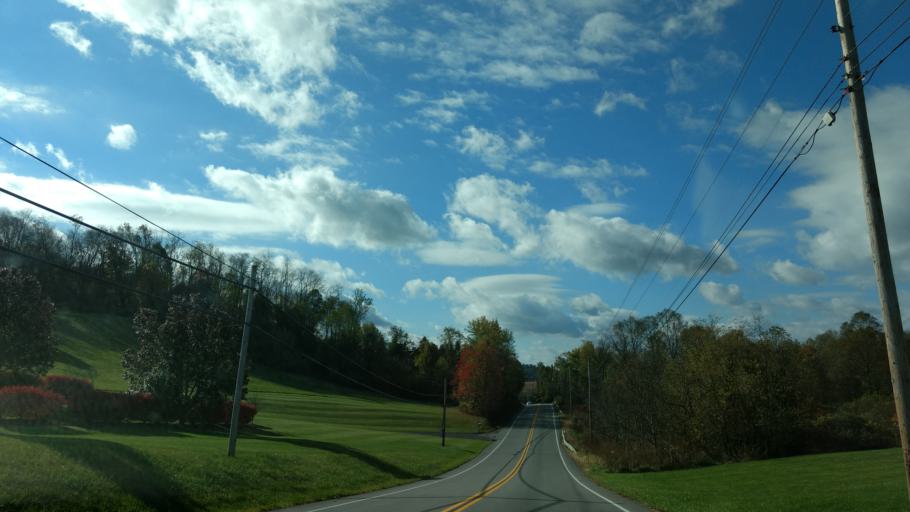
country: US
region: Pennsylvania
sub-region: Westmoreland County
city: Fellsburg
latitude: 40.1629
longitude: -79.8195
